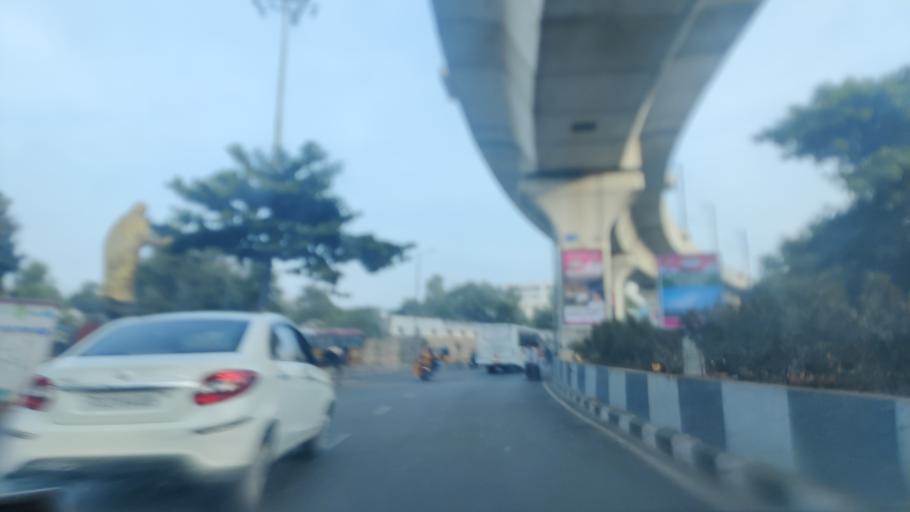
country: IN
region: Telangana
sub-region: Hyderabad
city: Malkajgiri
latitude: 17.4376
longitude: 78.5047
